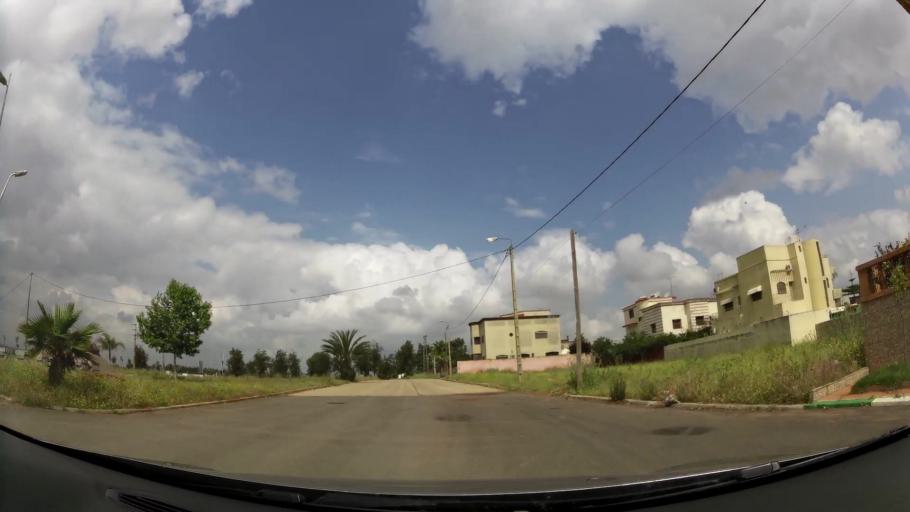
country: MA
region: Rabat-Sale-Zemmour-Zaer
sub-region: Khemisset
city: Tiflet
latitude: 33.8959
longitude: -6.3408
